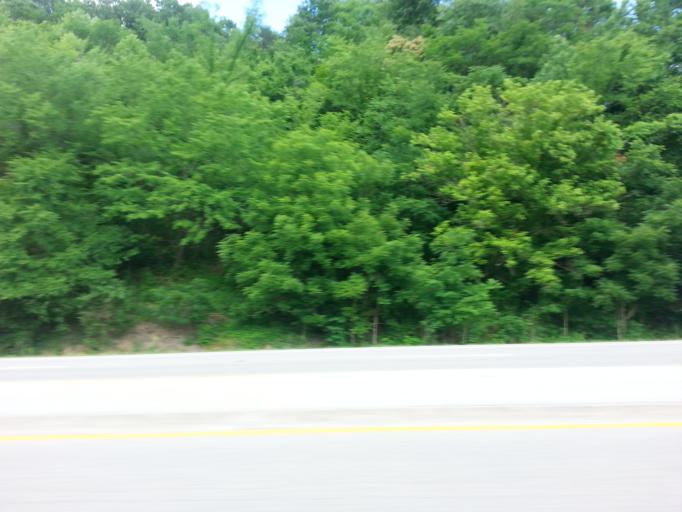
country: US
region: Kentucky
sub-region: Harlan County
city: Harlan
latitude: 36.8654
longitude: -83.3164
